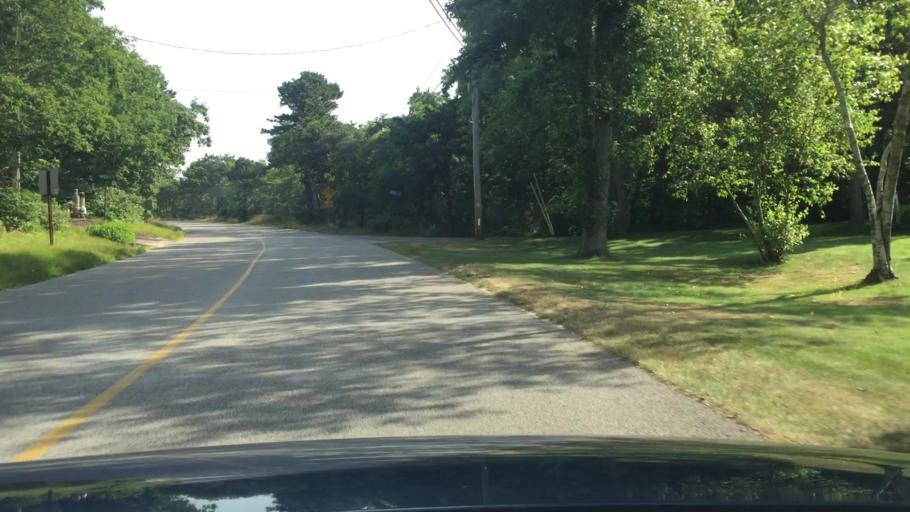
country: US
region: Massachusetts
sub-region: Barnstable County
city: Truro
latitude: 42.0249
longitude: -70.0693
